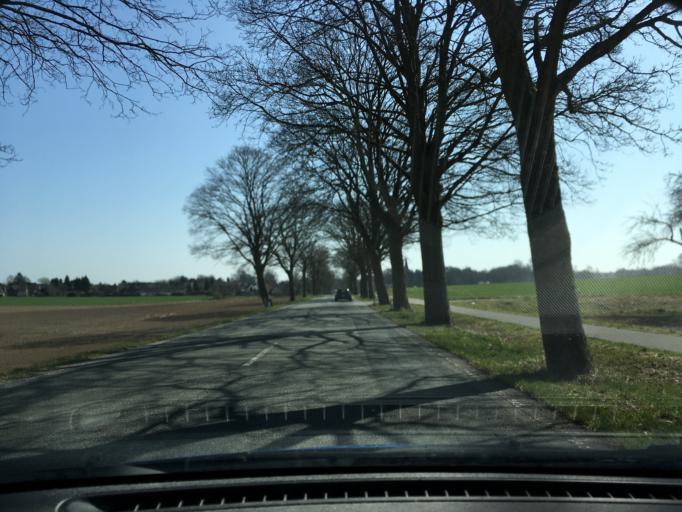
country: DE
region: Lower Saxony
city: Wriedel
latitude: 53.0397
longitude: 10.2973
